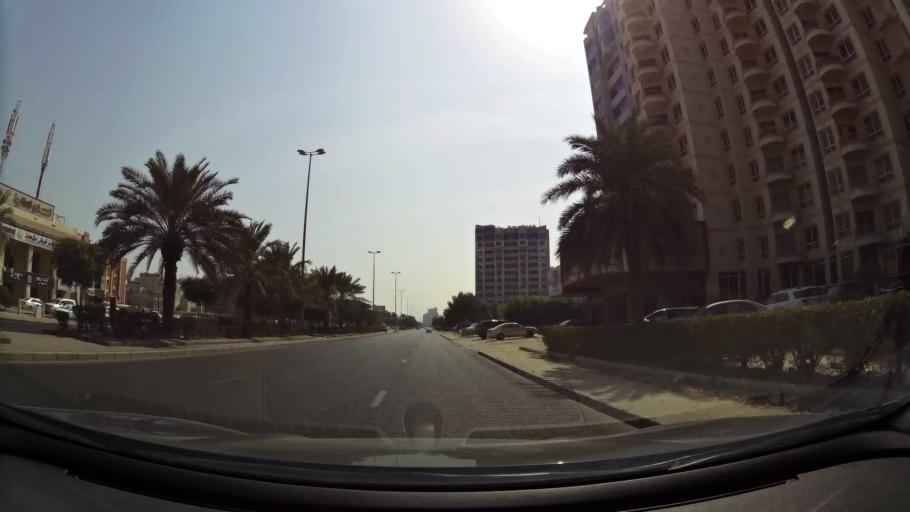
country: KW
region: Al Ahmadi
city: Al Mahbulah
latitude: 29.1437
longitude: 48.1289
